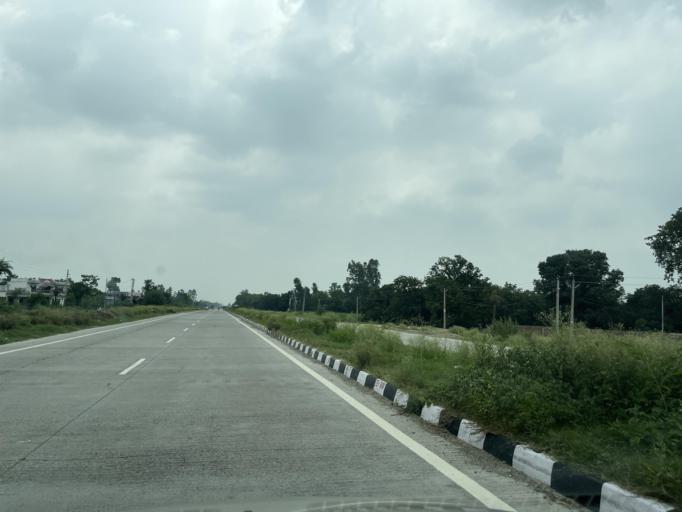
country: IN
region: Uttar Pradesh
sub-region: Bijnor
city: Najibabad
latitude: 29.5482
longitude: 78.3396
